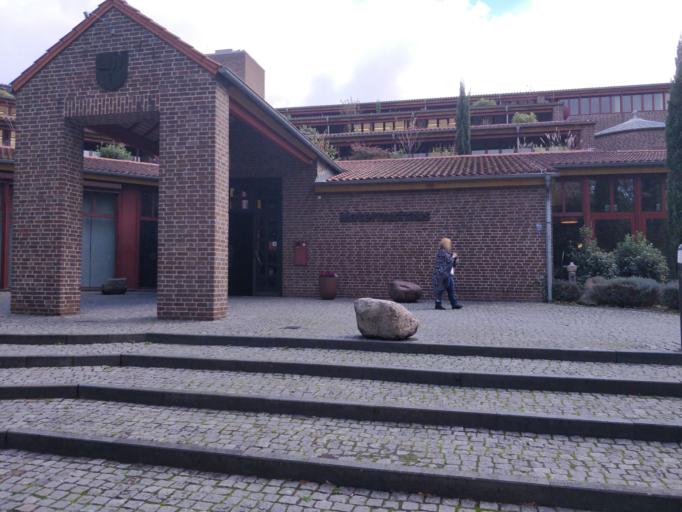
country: DE
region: North Rhine-Westphalia
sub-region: Regierungsbezirk Koln
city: Neustadt/Nord
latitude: 50.9447
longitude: 6.9517
